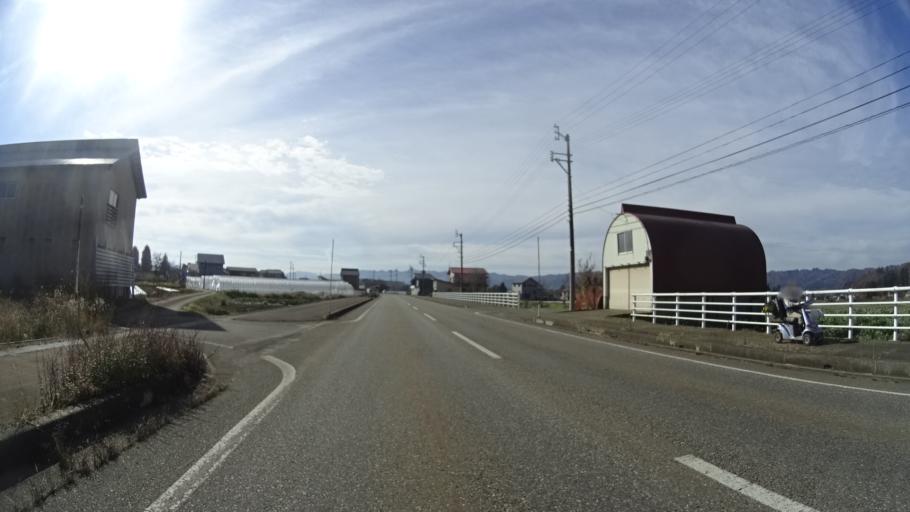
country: JP
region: Niigata
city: Muikamachi
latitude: 37.1784
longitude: 138.9729
